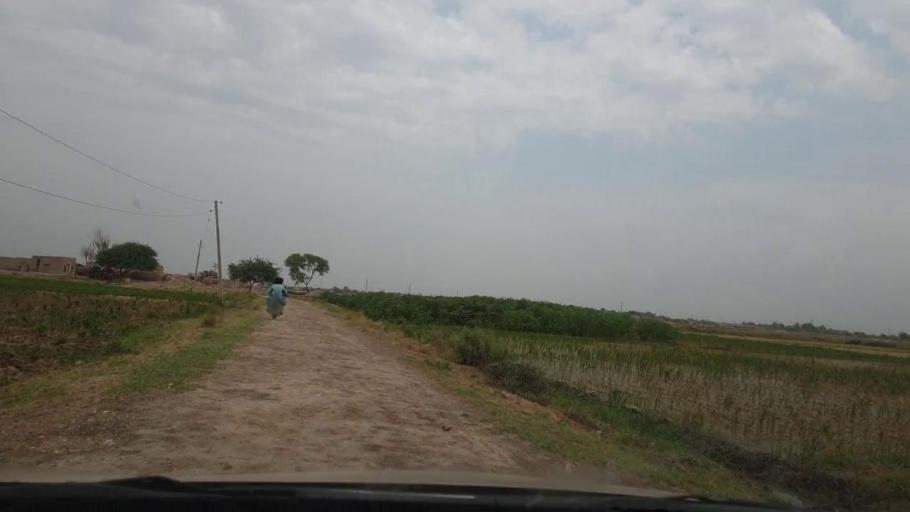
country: PK
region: Sindh
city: Ratodero
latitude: 27.7749
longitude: 68.2780
